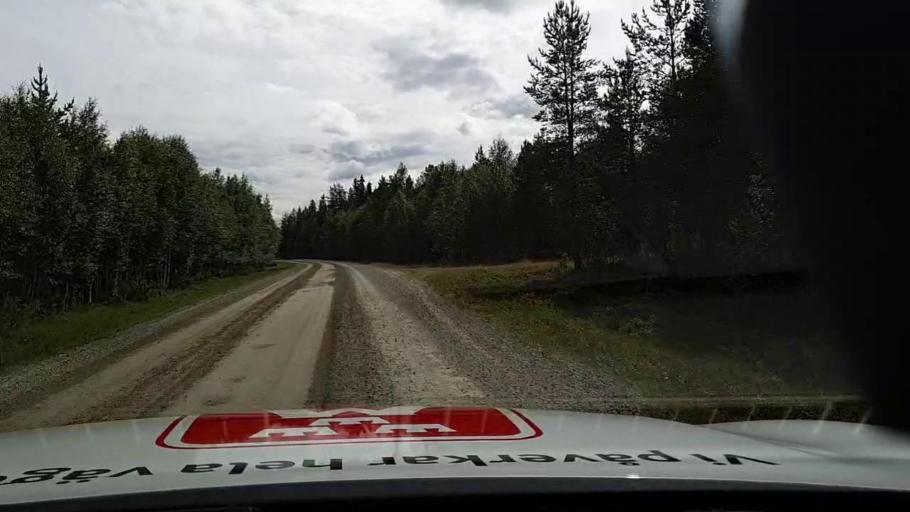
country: SE
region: Jaemtland
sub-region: Are Kommun
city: Jarpen
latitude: 62.5219
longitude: 13.4880
